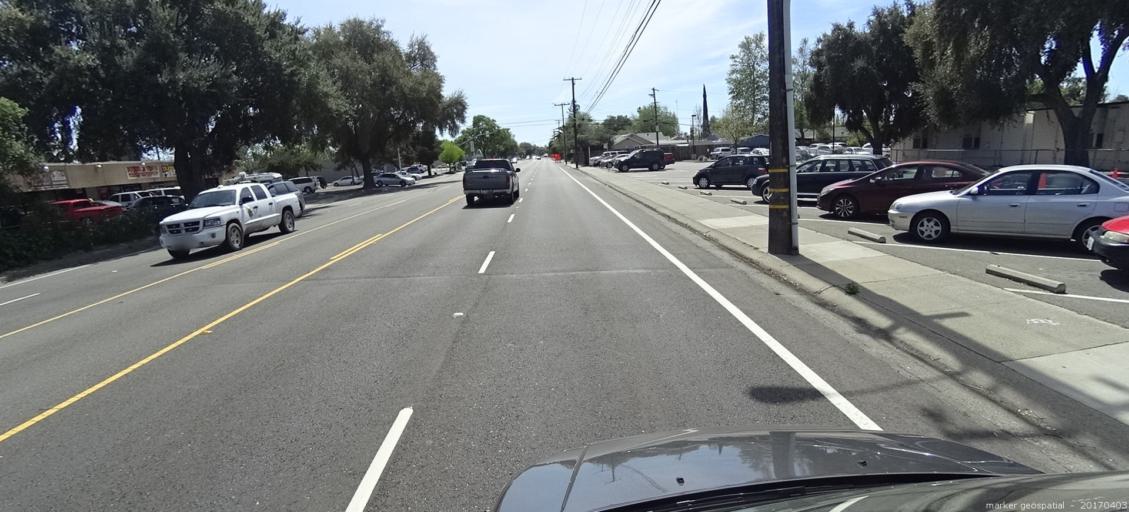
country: US
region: California
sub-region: Sacramento County
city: Sacramento
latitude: 38.6148
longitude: -121.4756
